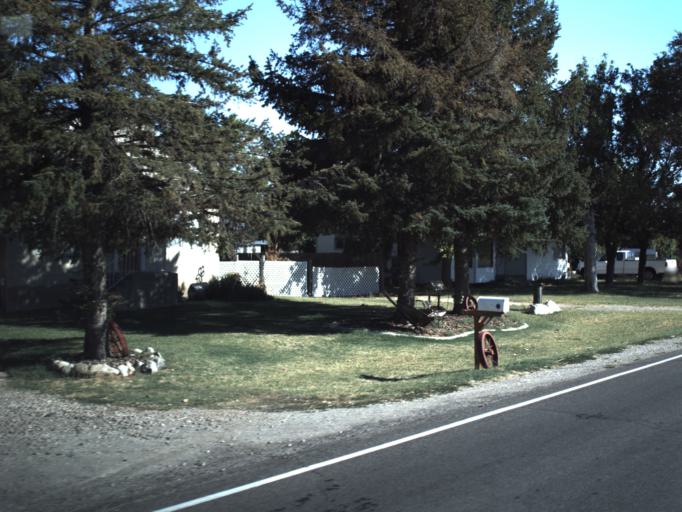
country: US
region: Utah
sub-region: Weber County
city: Hooper
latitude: 41.1827
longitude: -112.1227
